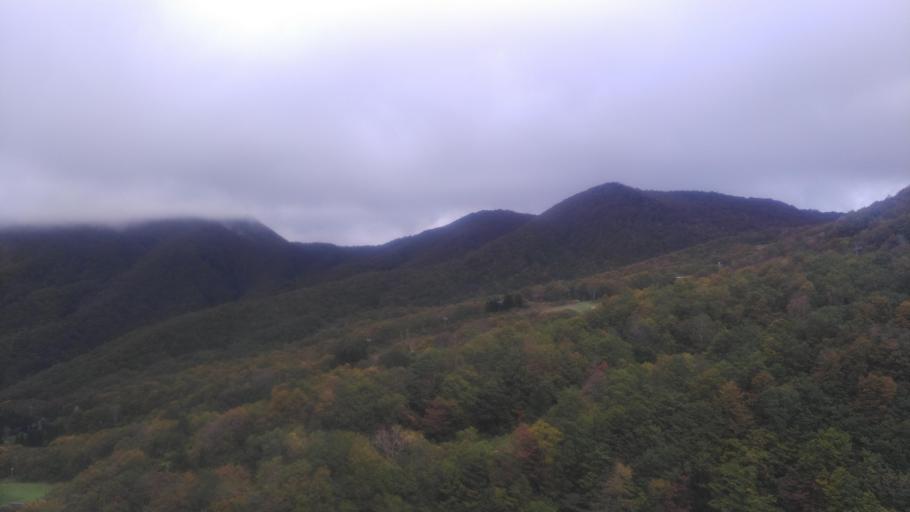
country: JP
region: Yamagata
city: Yamagata-shi
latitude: 38.1655
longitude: 140.4078
